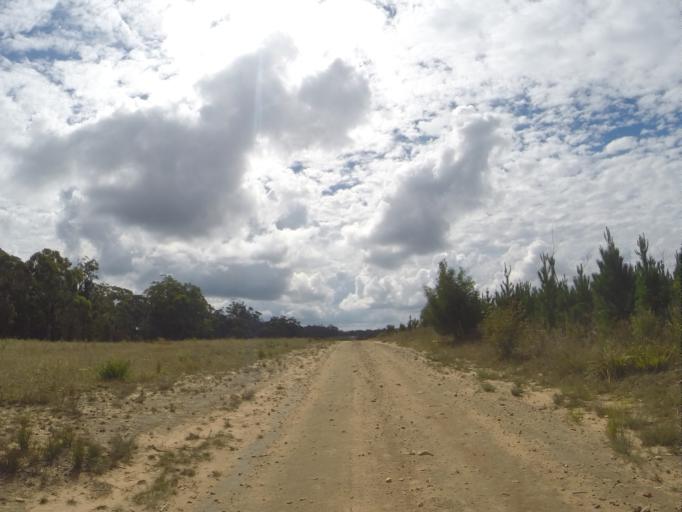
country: AU
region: New South Wales
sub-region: Wingecarribee
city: Moss Vale
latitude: -34.5136
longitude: 150.2272
